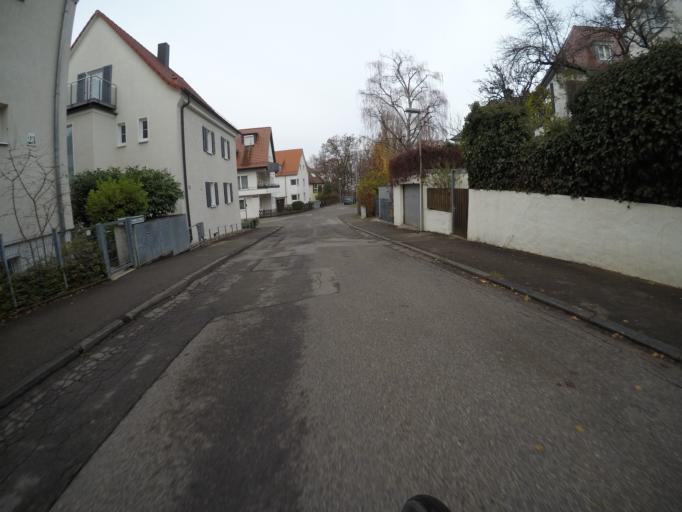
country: DE
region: Baden-Wuerttemberg
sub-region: Regierungsbezirk Stuttgart
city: Stuttgart
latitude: 48.7520
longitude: 9.1695
